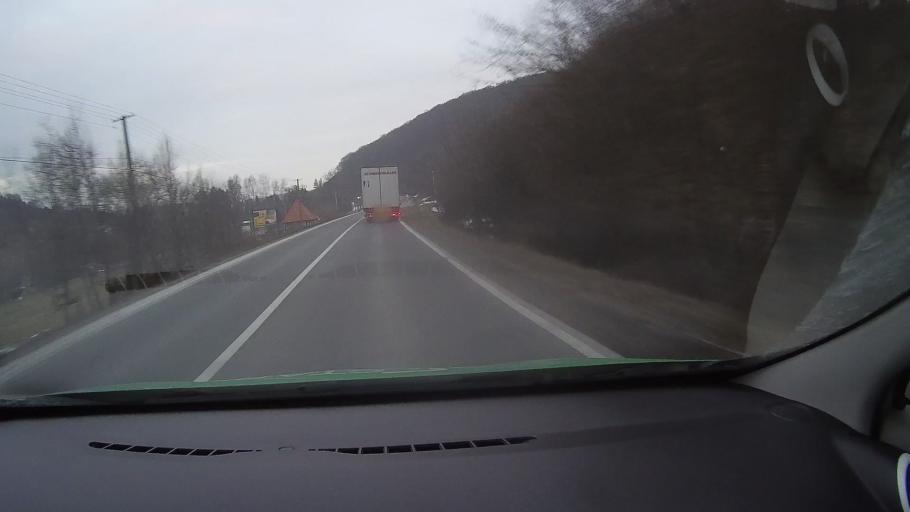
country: RO
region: Harghita
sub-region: Municipiul Odorheiu Secuiesc
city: Odorheiu Secuiesc
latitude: 46.3350
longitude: 25.2709
